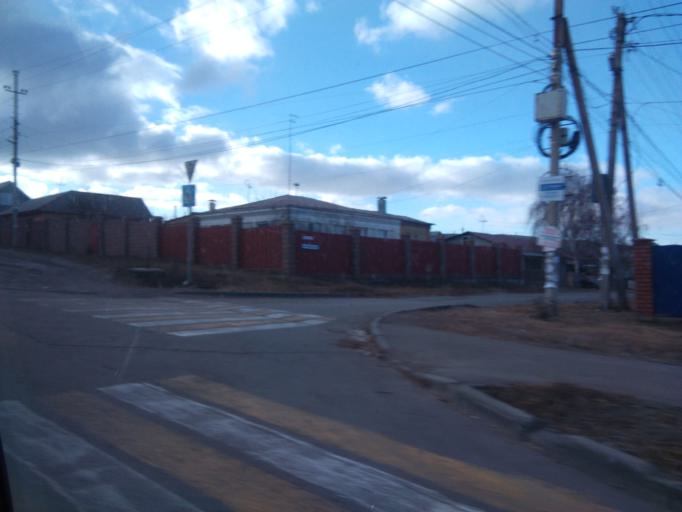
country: RU
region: Chelyabinsk
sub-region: Gorod Magnitogorsk
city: Magnitogorsk
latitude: 53.3882
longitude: 59.0524
